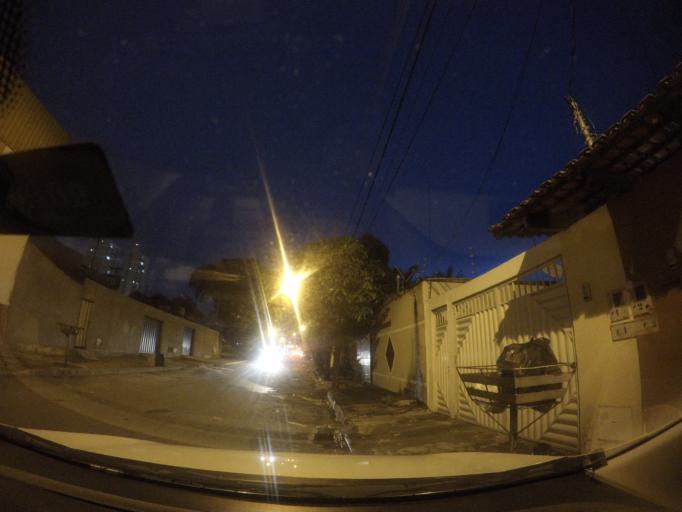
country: BR
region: Goias
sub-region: Goiania
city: Goiania
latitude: -16.6620
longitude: -49.3082
